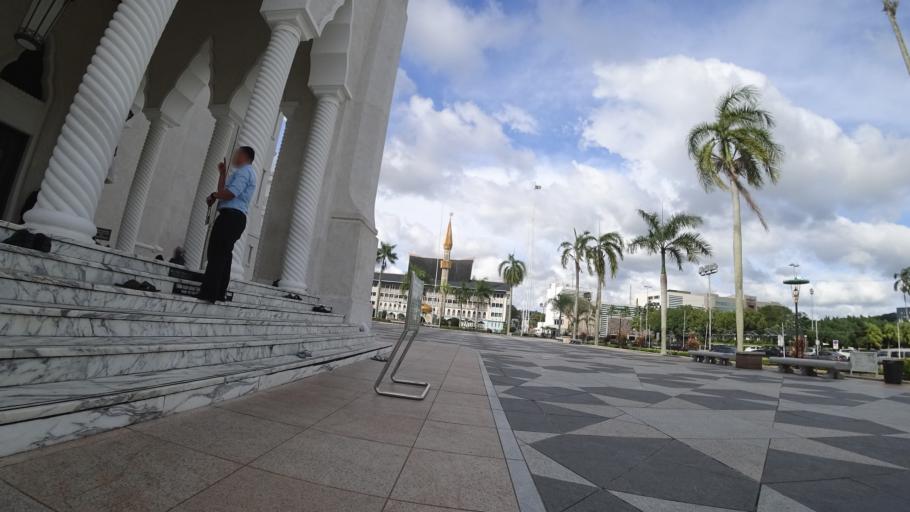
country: BN
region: Brunei and Muara
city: Bandar Seri Begawan
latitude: 4.8894
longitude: 114.9395
